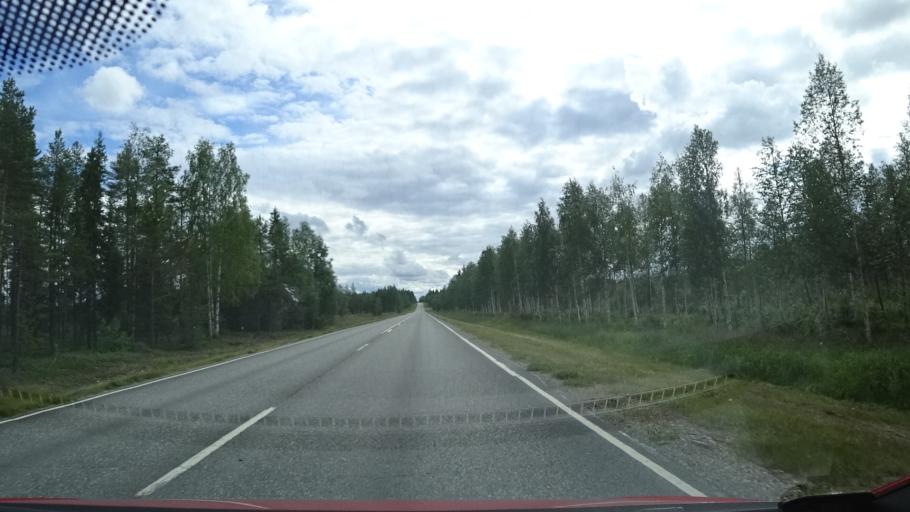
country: FI
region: Lapland
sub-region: Tunturi-Lappi
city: Kittilae
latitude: 67.4786
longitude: 24.9313
